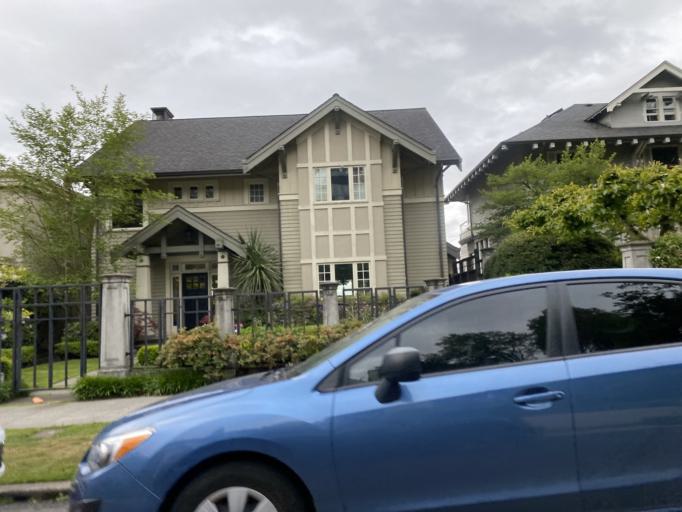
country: US
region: Washington
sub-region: King County
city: Seattle
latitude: 47.6288
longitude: -122.3615
